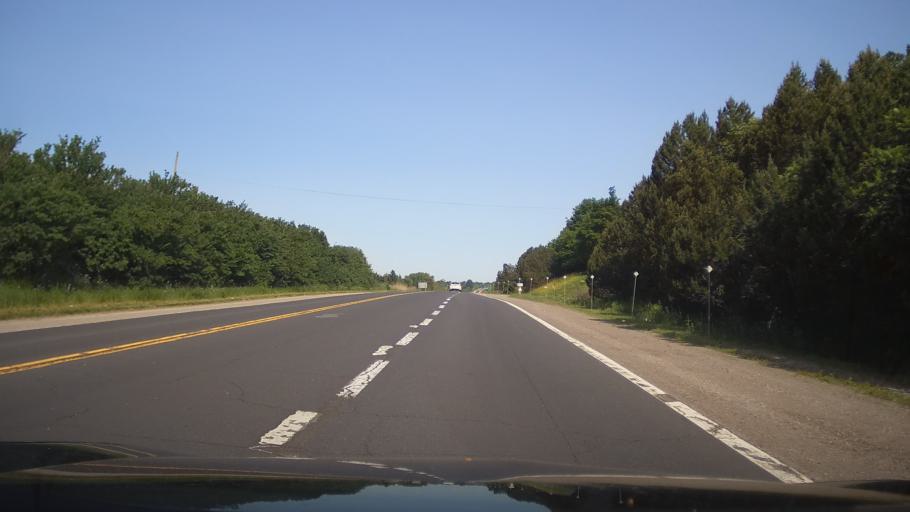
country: CA
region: Ontario
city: Omemee
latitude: 44.2935
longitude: -78.5930
